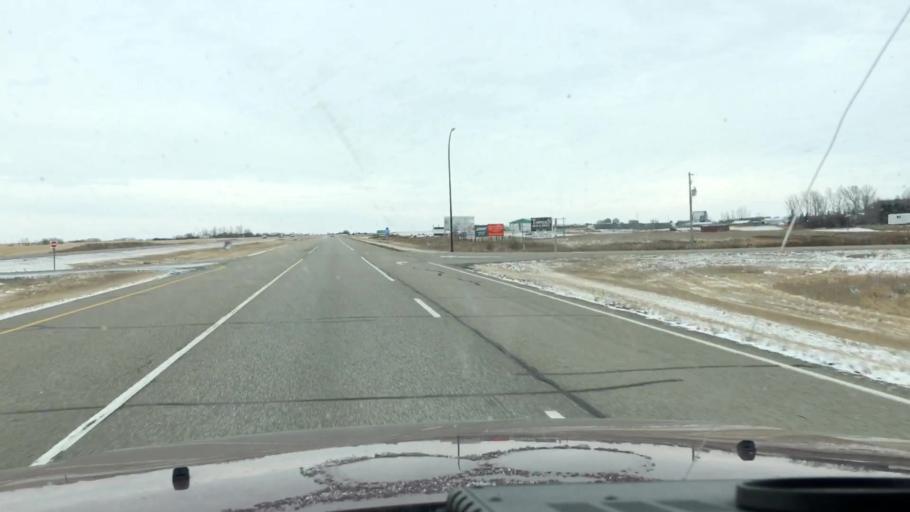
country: CA
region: Saskatchewan
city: Watrous
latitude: 51.3689
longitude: -106.1352
